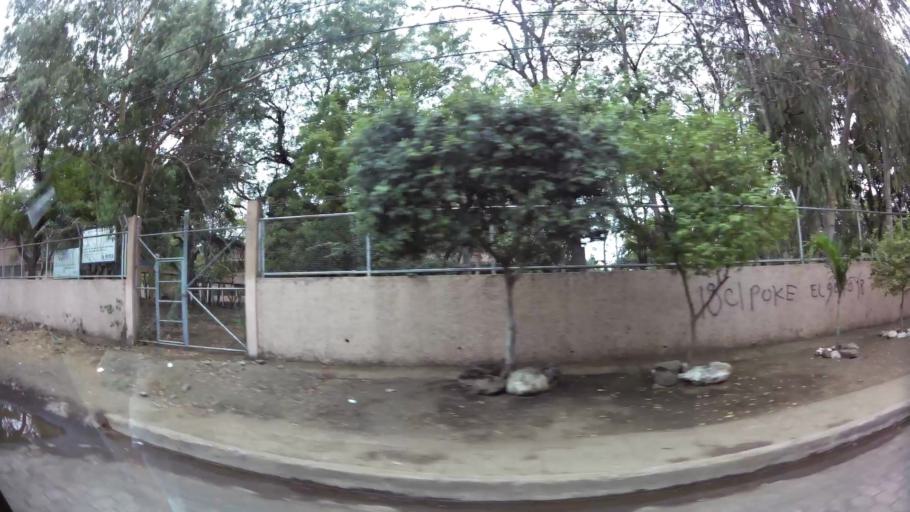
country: NI
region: Chinandega
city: Chinandega
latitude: 12.6165
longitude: -87.1153
